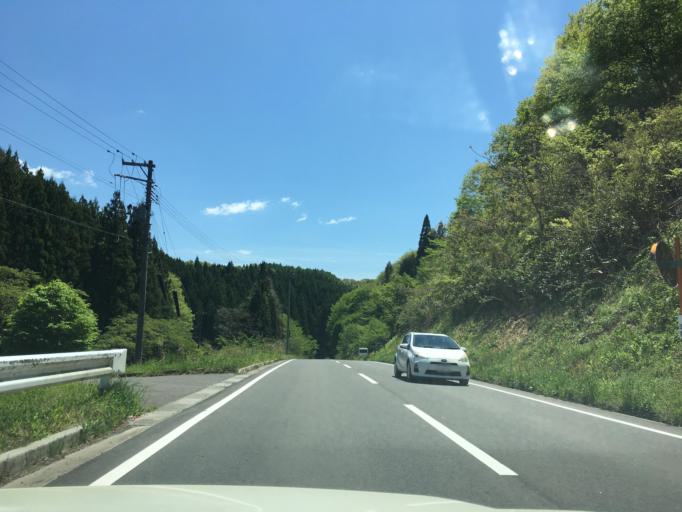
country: JP
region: Fukushima
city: Funehikimachi-funehiki
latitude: 37.3346
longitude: 140.6257
